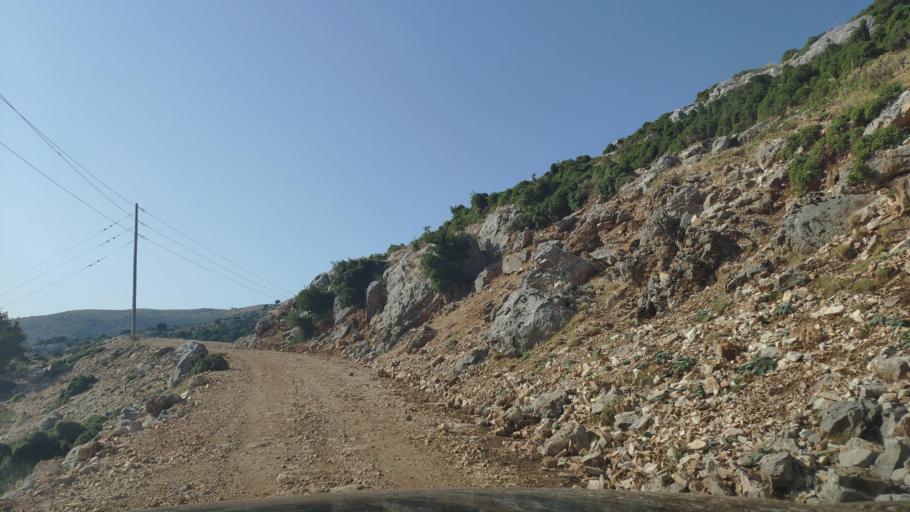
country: GR
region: West Greece
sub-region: Nomos Aitolias kai Akarnanias
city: Monastirakion
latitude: 38.8265
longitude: 20.9796
